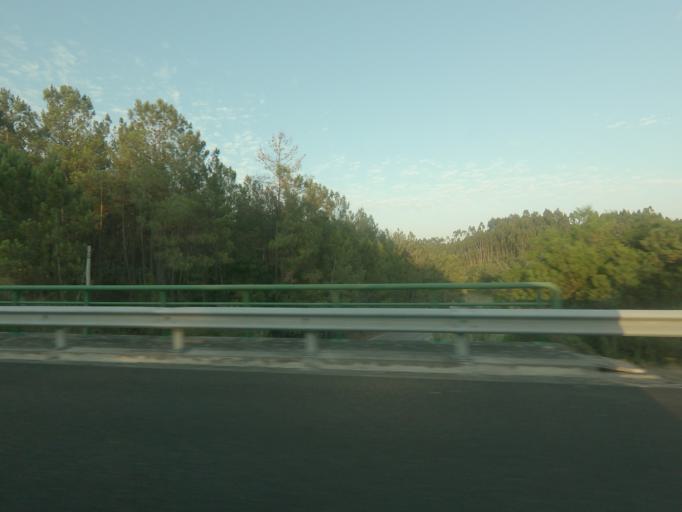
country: PT
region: Leiria
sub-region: Leiria
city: Caranguejeira
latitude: 39.7864
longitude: -8.7369
